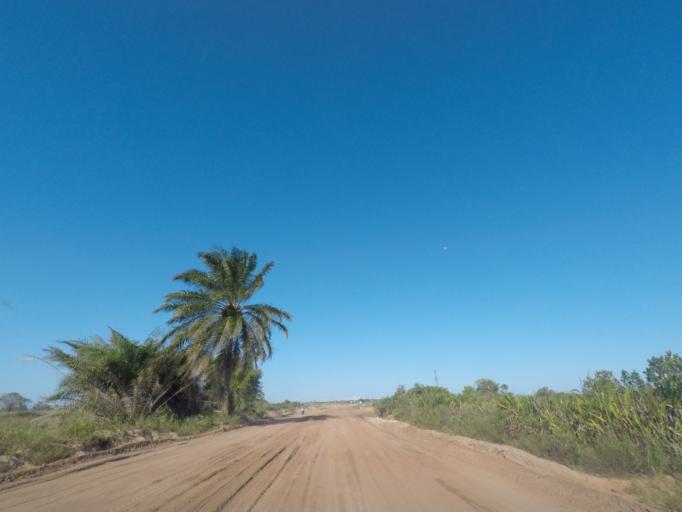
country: BR
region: Bahia
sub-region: Camamu
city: Camamu
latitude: -13.9430
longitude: -38.9474
